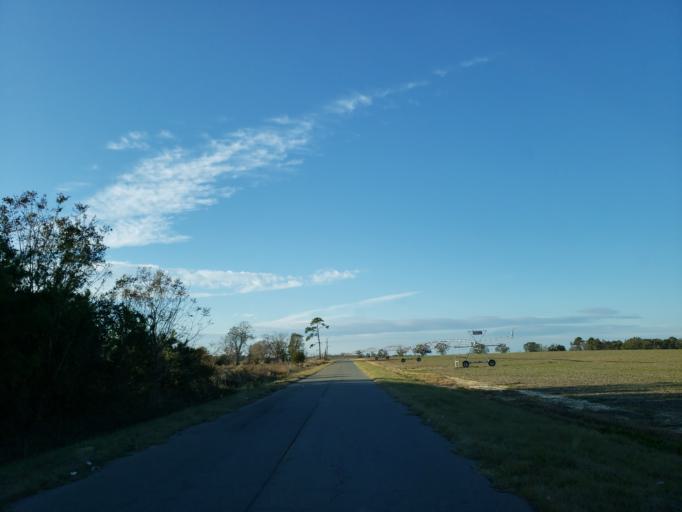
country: US
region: Georgia
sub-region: Dooly County
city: Unadilla
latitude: 32.2018
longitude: -83.7677
